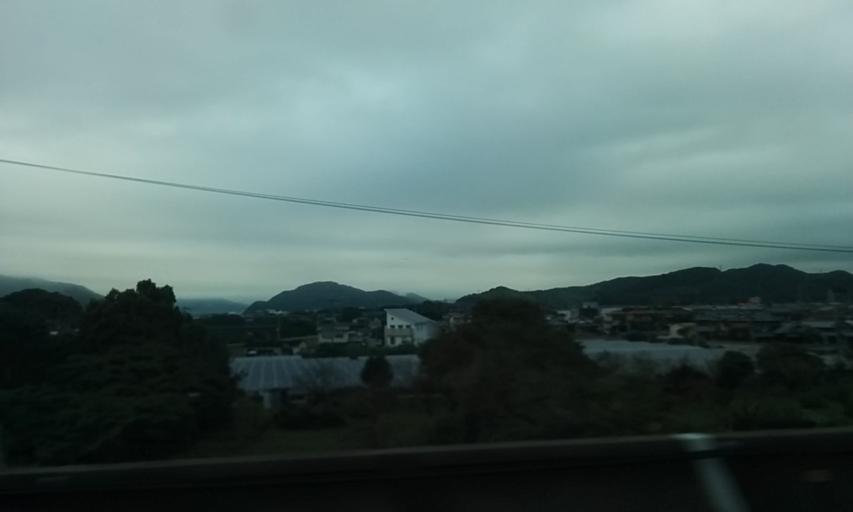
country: JP
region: Hyogo
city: Tatsunocho-tominaga
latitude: 34.8301
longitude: 134.5613
